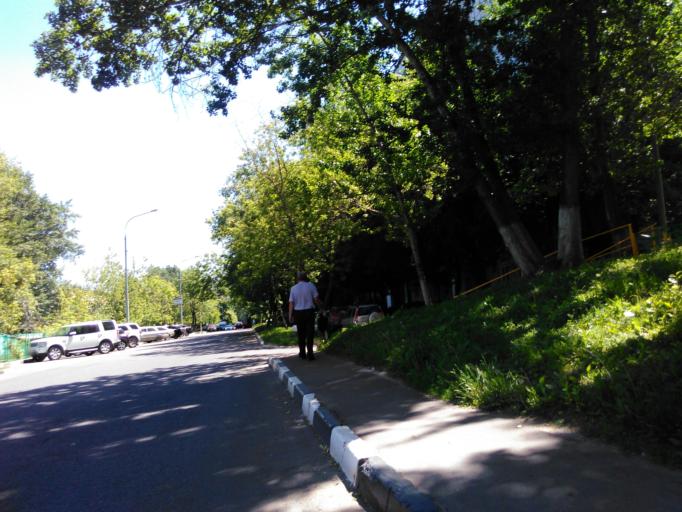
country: RU
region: Moscow
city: Zyuzino
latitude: 55.6678
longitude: 37.5750
